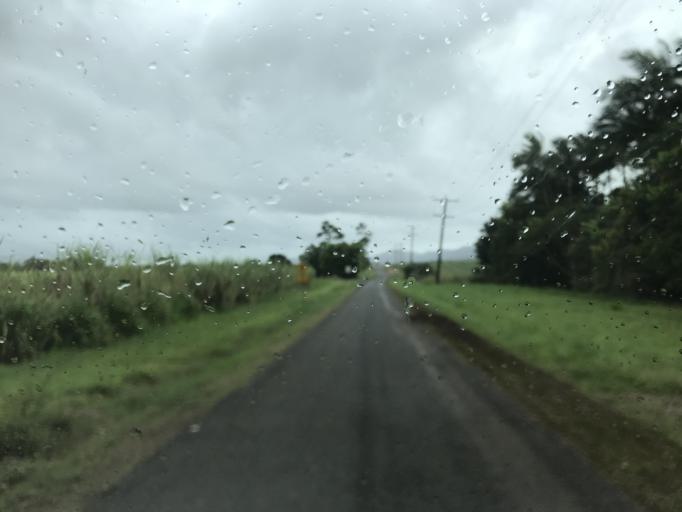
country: AU
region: Queensland
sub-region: Cassowary Coast
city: Innisfail
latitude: -17.4838
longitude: 145.9892
